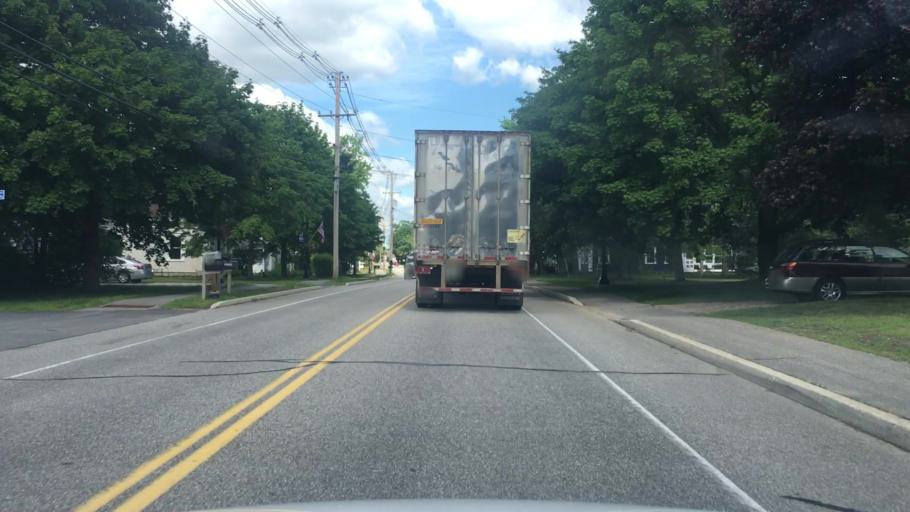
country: US
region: Maine
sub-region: York County
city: West Kennebunk
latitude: 43.4074
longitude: -70.5751
